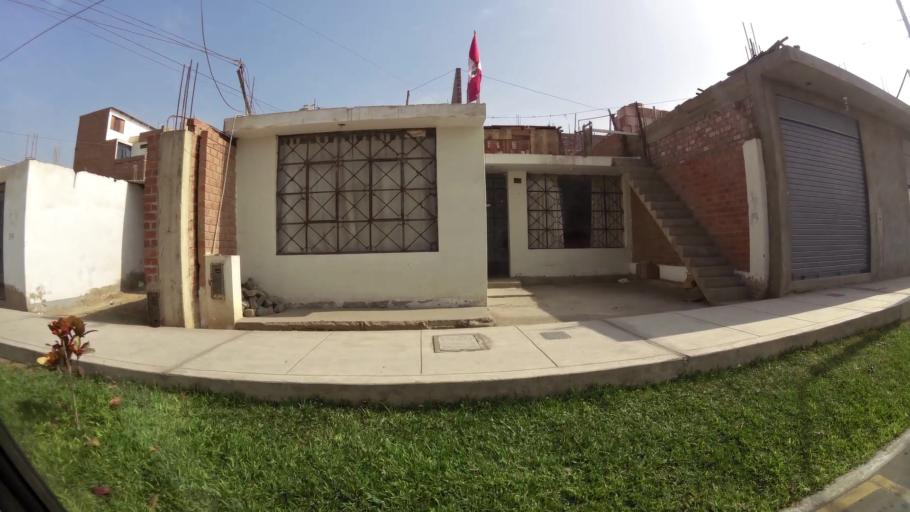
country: PE
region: Lima
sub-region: Lima
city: Santa Rosa
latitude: -11.7819
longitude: -77.1613
